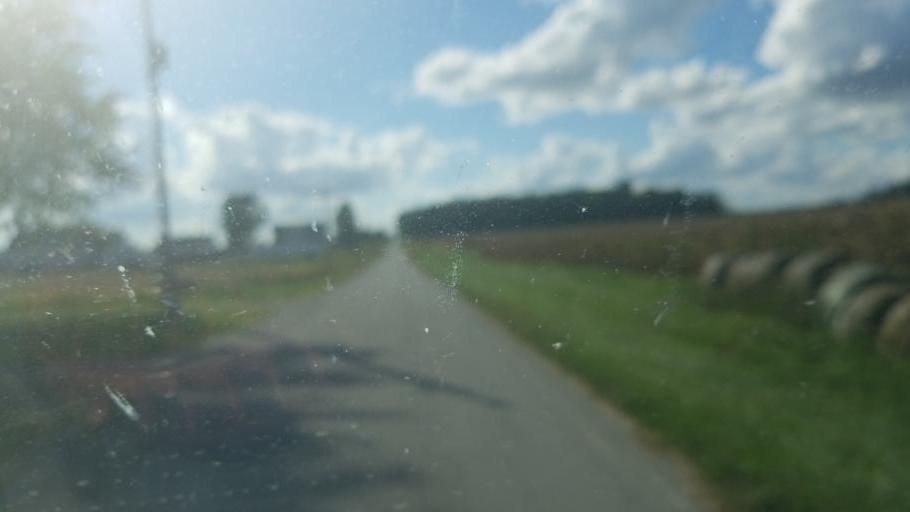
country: US
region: Ohio
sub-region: Hardin County
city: Ada
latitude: 40.7183
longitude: -83.7152
